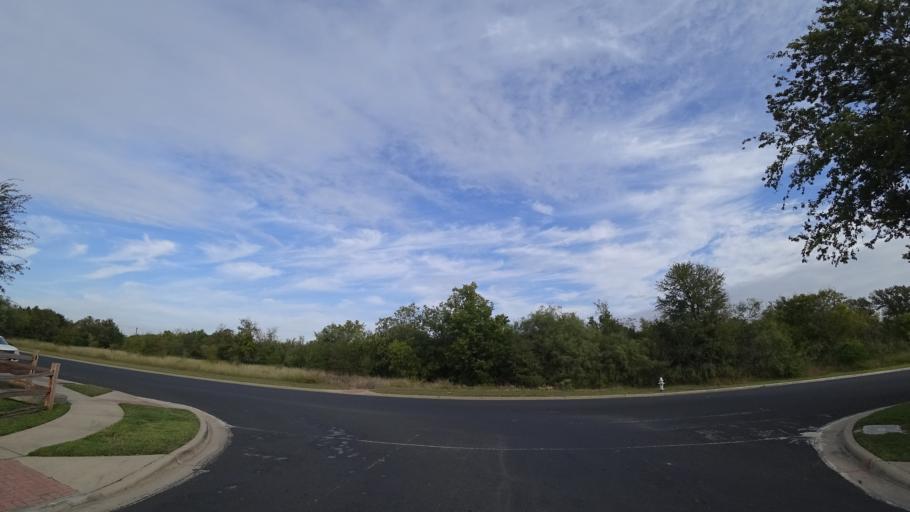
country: US
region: Texas
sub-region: Travis County
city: Austin
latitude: 30.2004
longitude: -97.7321
